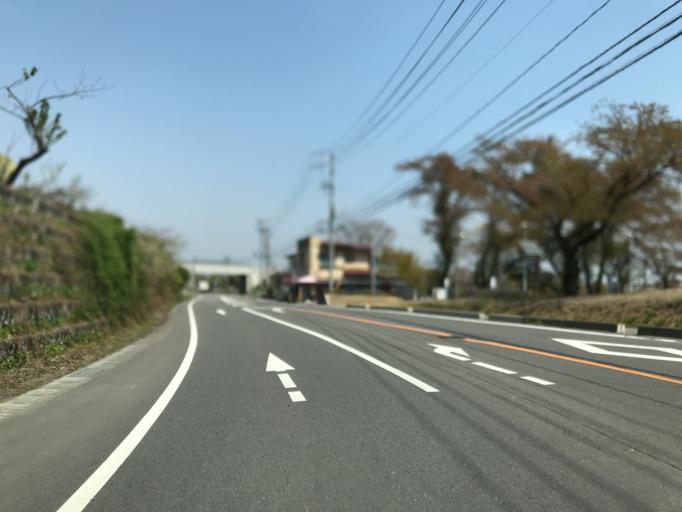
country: JP
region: Fukushima
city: Sukagawa
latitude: 37.1920
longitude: 140.3407
